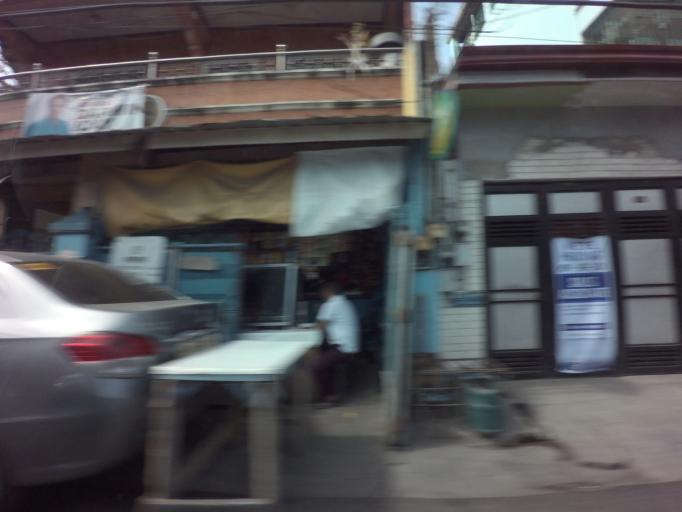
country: PH
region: Calabarzon
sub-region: Province of Rizal
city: Pateros
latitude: 14.5399
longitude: 121.0921
